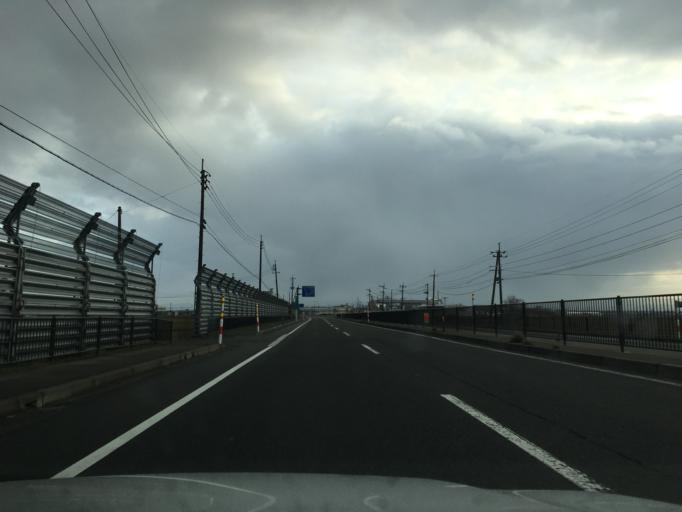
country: JP
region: Yamagata
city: Tsuruoka
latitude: 38.7221
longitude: 139.7688
